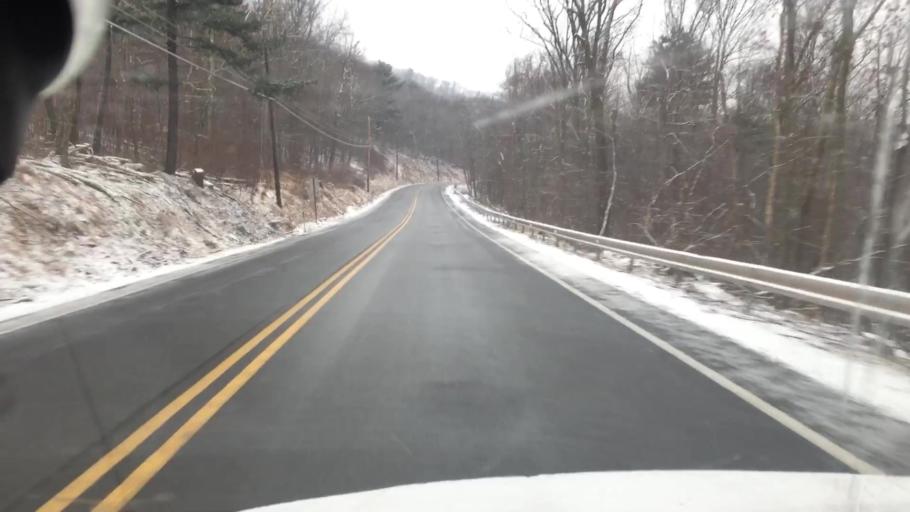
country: US
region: Pennsylvania
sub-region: Luzerne County
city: Conyngham
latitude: 41.0326
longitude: -76.1221
